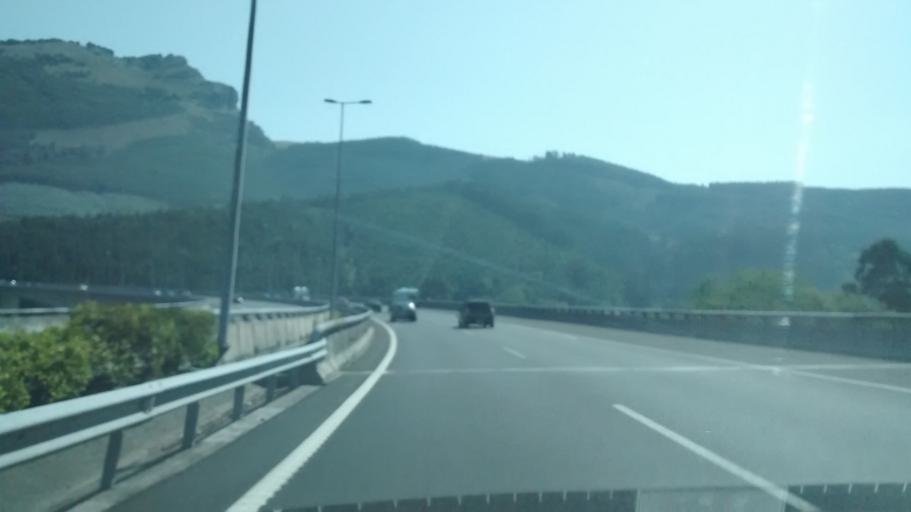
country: ES
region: Cantabria
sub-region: Provincia de Cantabria
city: Liendo
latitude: 43.3848
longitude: -3.3236
